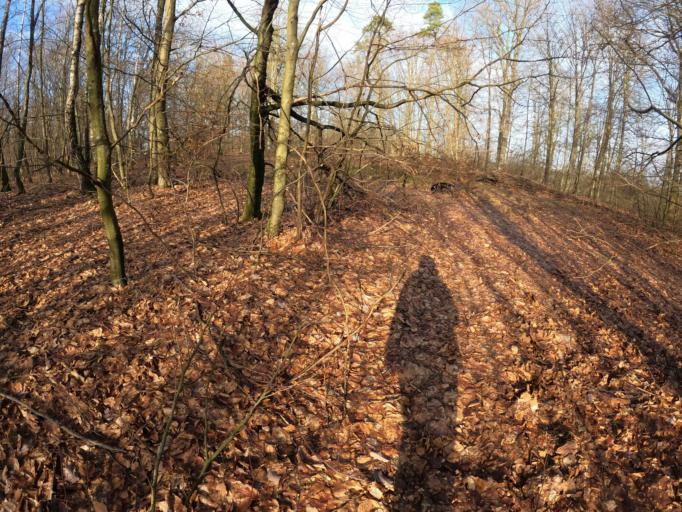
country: PL
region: West Pomeranian Voivodeship
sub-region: Powiat koszalinski
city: Polanow
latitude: 54.1211
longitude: 16.7007
